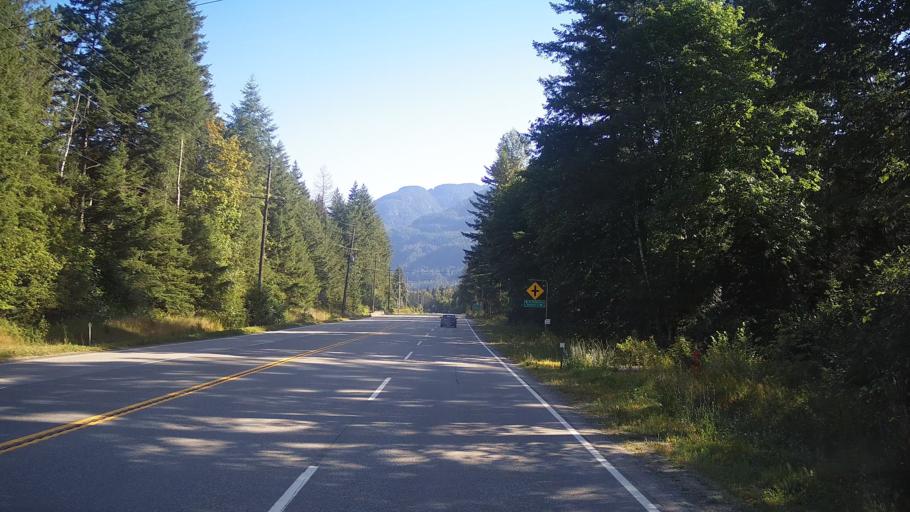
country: CA
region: British Columbia
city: Hope
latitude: 49.4731
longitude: -121.4272
